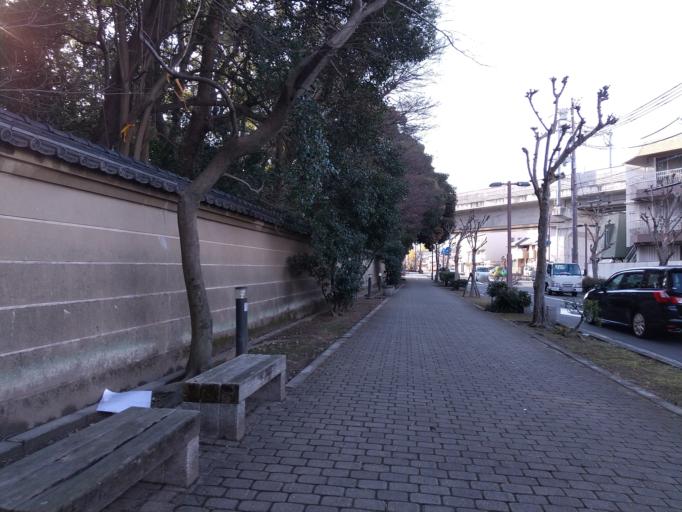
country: JP
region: Hyogo
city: Nishinomiya-hama
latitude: 34.7364
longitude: 135.3346
